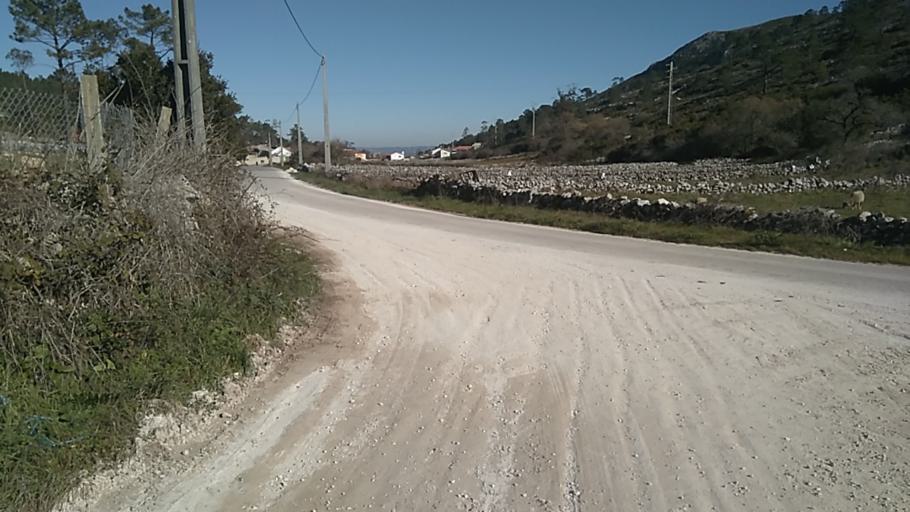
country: PT
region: Leiria
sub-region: Porto de Mos
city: Porto de Mos
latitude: 39.5358
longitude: -8.8563
